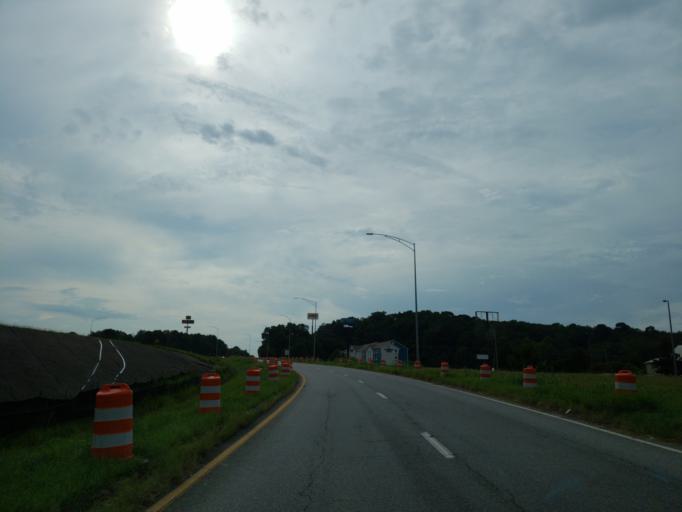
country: US
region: Alabama
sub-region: Tuscaloosa County
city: Holt
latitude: 33.1749
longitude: -87.4742
